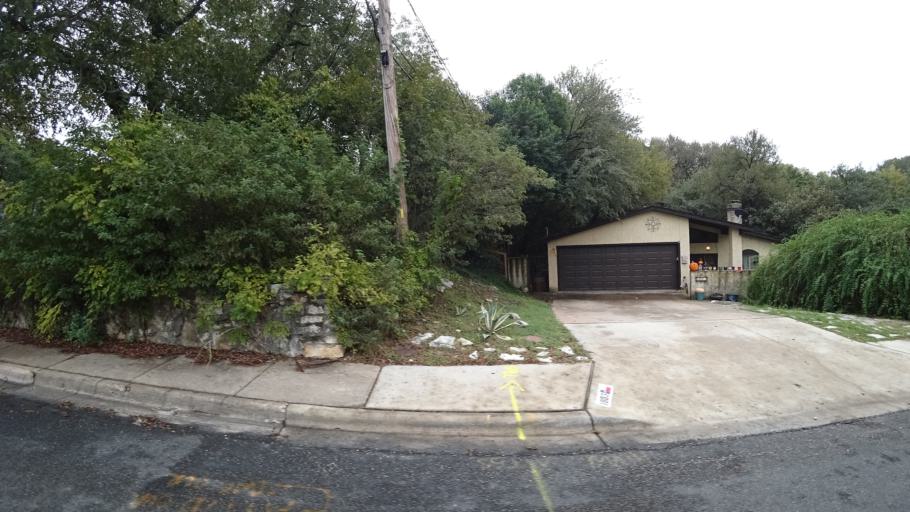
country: US
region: Texas
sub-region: Travis County
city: Rollingwood
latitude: 30.2580
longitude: -97.7805
